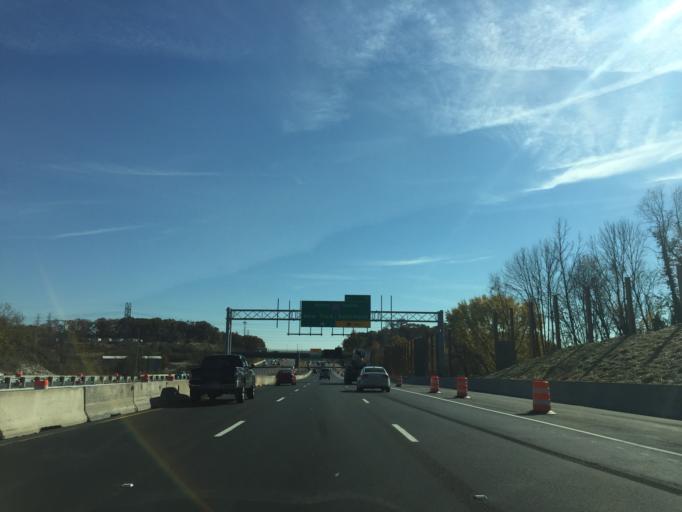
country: US
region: Maryland
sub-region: Baltimore County
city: Overlea
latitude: 39.3642
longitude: -76.5080
